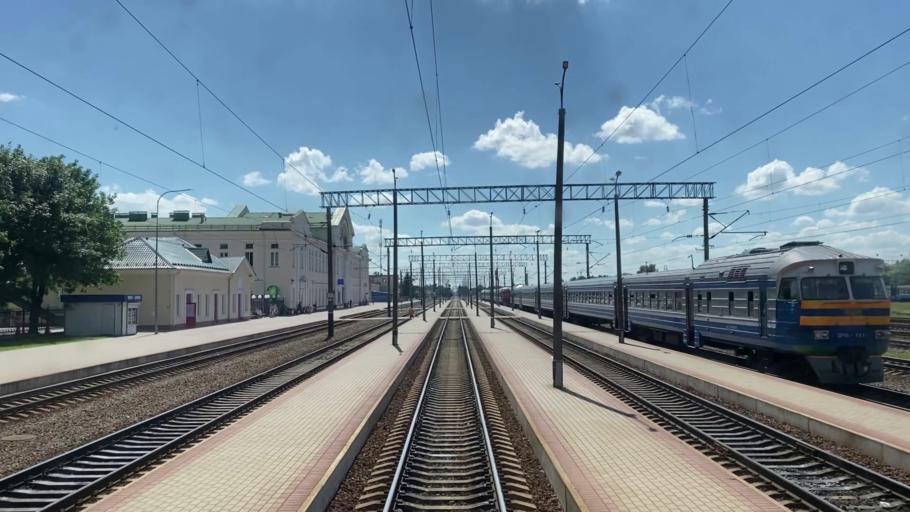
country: BY
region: Brest
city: Baranovichi
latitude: 53.1304
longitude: 26.0410
